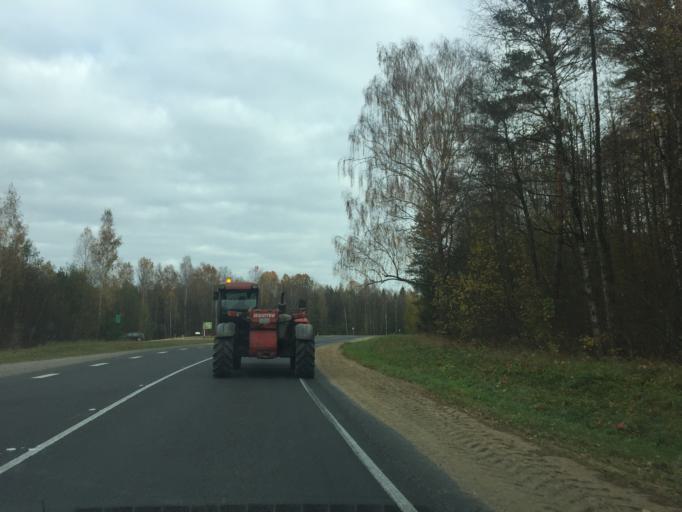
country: BY
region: Minsk
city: Svir
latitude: 54.8497
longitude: 26.2109
